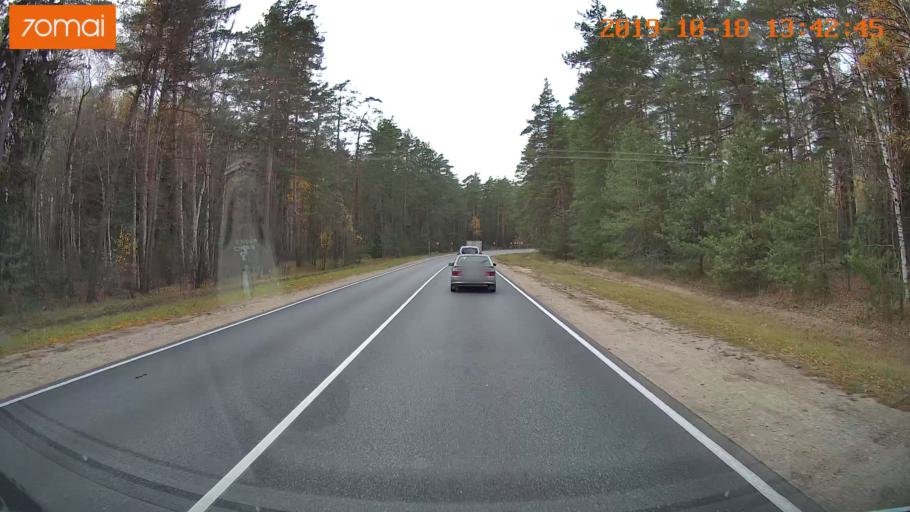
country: RU
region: Rjazan
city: Solotcha
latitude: 54.9270
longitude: 39.9839
